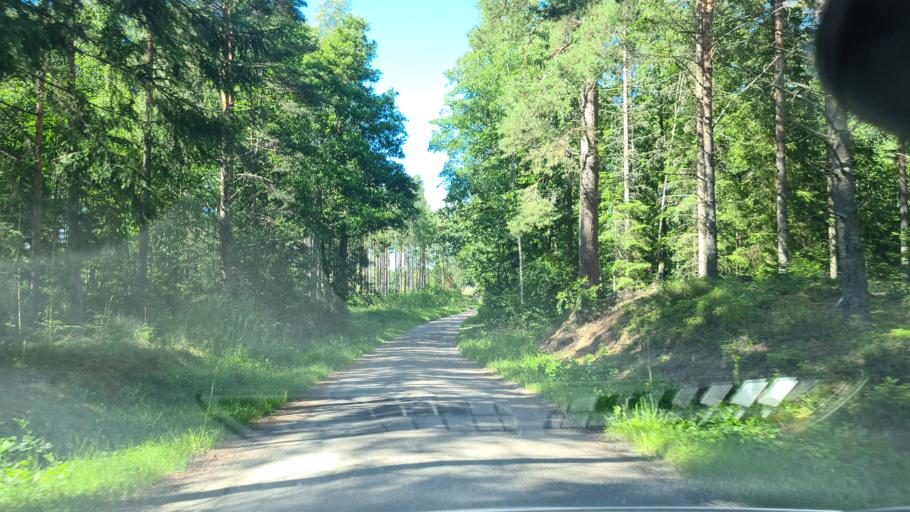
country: SE
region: OEstergoetland
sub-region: Norrkopings Kommun
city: Krokek
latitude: 58.6968
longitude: 16.4272
